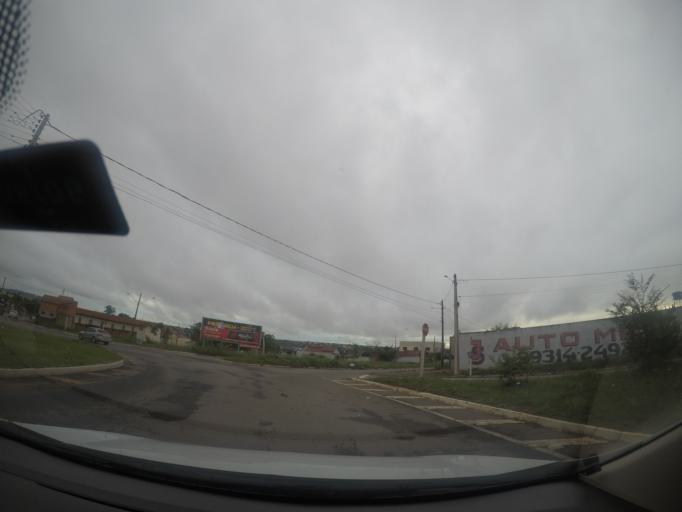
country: BR
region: Goias
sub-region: Goiania
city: Goiania
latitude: -16.7534
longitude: -49.3222
